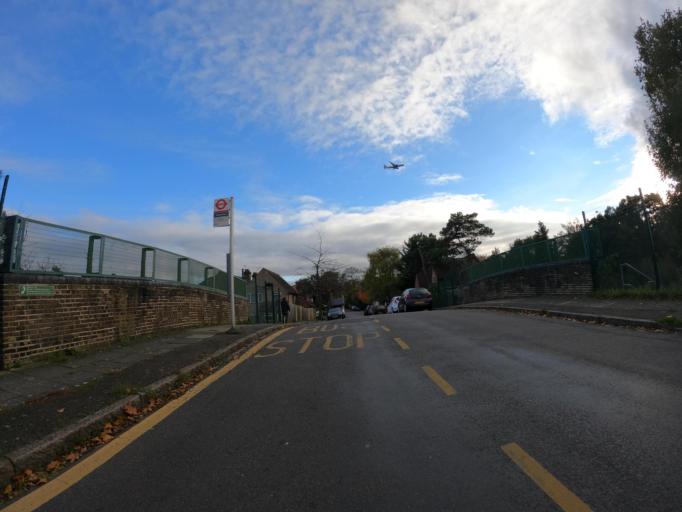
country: GB
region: England
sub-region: Greater London
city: Isleworth
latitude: 51.4845
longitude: -0.3427
